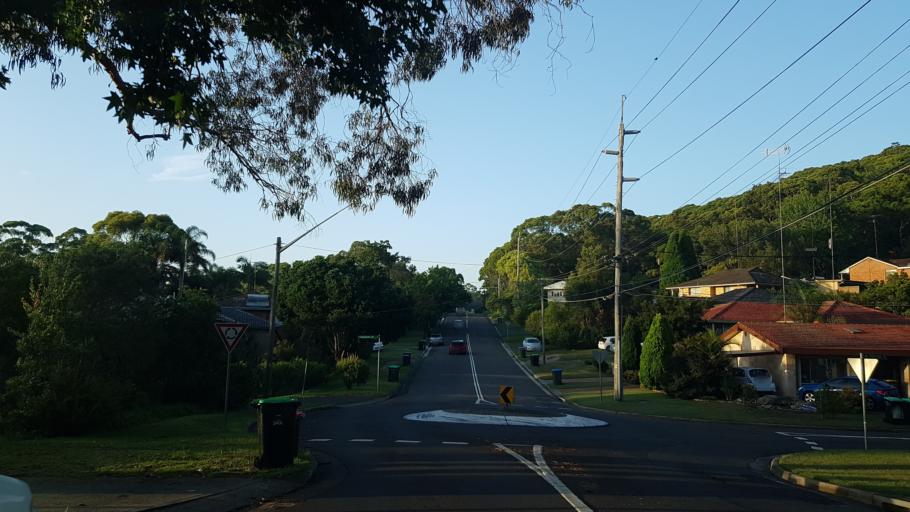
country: AU
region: New South Wales
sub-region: Warringah
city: Narraweena
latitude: -33.7372
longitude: 151.2710
